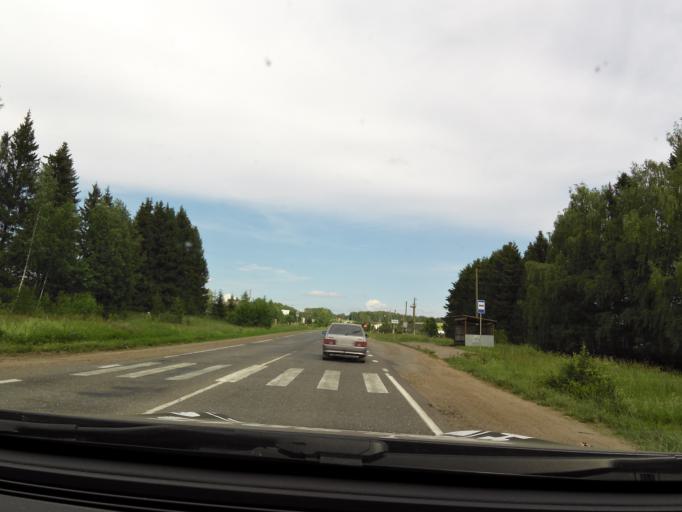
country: RU
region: Kirov
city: Vakhrushi
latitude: 58.6572
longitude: 49.9099
